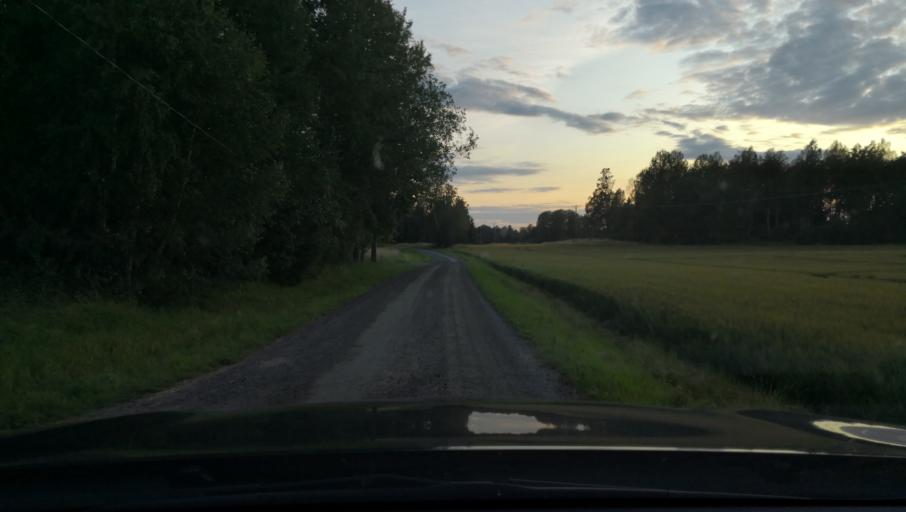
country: SE
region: Uppsala
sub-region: Osthammars Kommun
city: Bjorklinge
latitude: 60.0536
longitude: 17.6368
